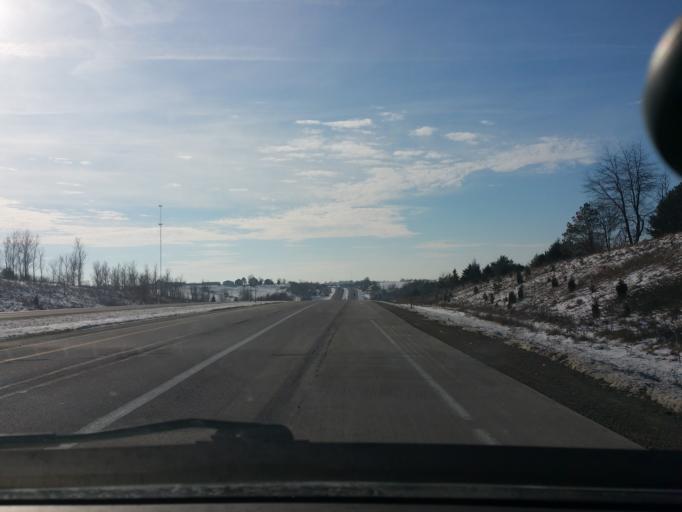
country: US
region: Iowa
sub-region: Warren County
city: Norwalk
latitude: 41.4449
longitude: -93.7801
